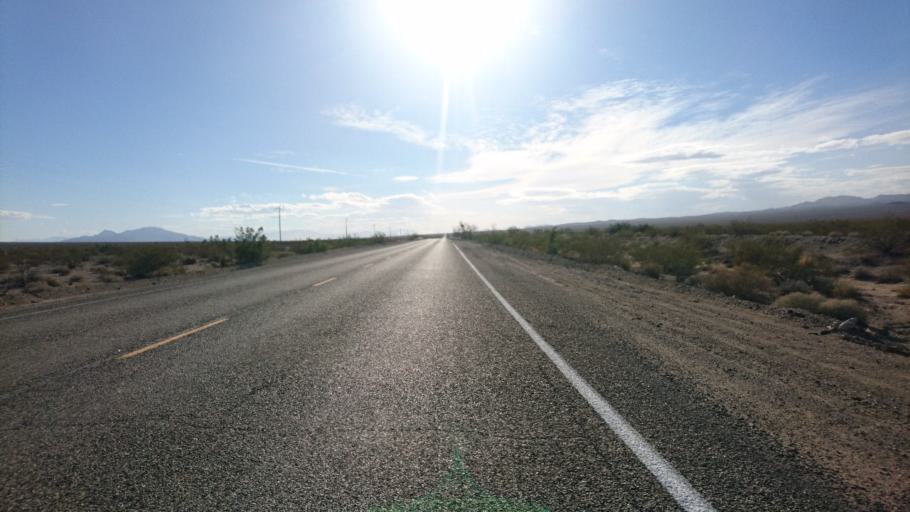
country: US
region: California
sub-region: San Bernardino County
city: Needles
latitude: 34.7029
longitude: -115.2946
